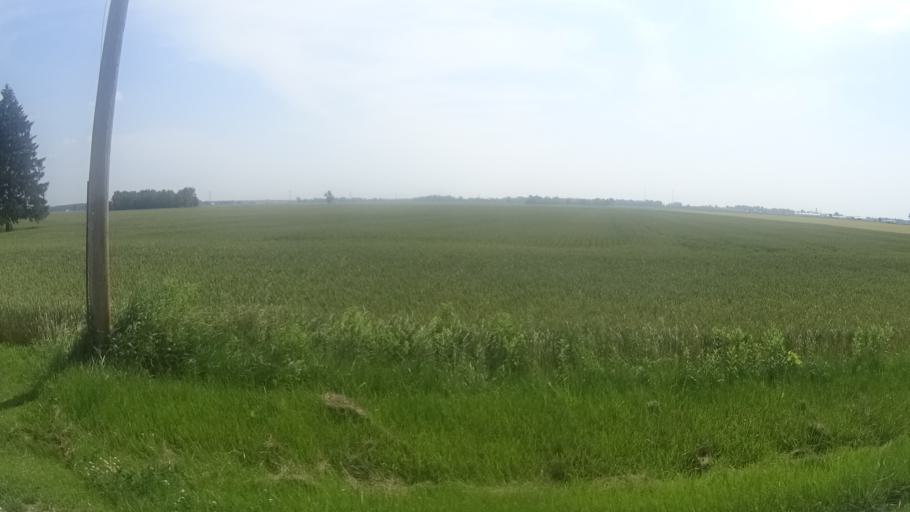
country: US
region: Ohio
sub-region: Huron County
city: Monroeville
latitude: 41.3392
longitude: -82.7228
